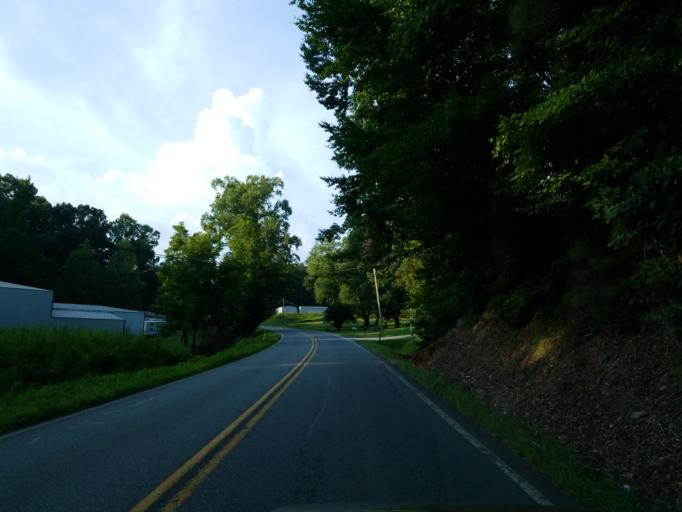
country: US
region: Georgia
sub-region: Gilmer County
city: Ellijay
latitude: 34.6242
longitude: -84.5171
